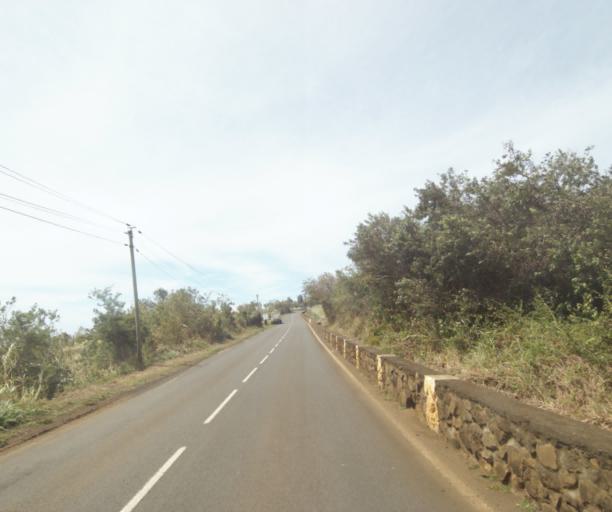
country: RE
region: Reunion
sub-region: Reunion
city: Saint-Paul
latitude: -21.0408
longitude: 55.2878
